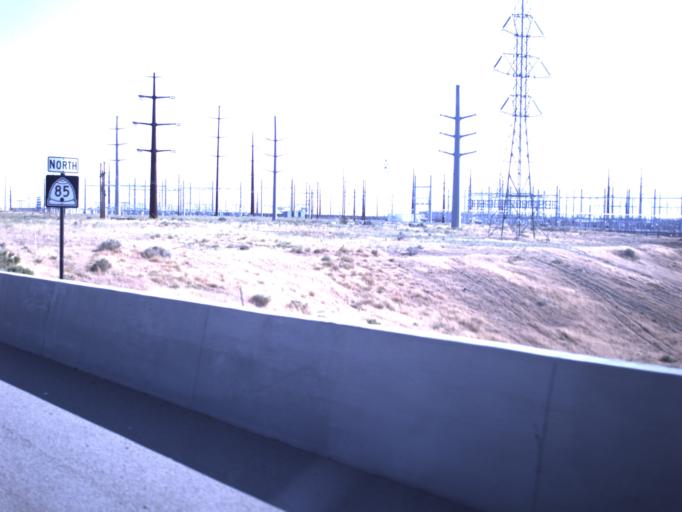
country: US
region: Utah
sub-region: Salt Lake County
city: Herriman
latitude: 40.5622
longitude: -112.0313
